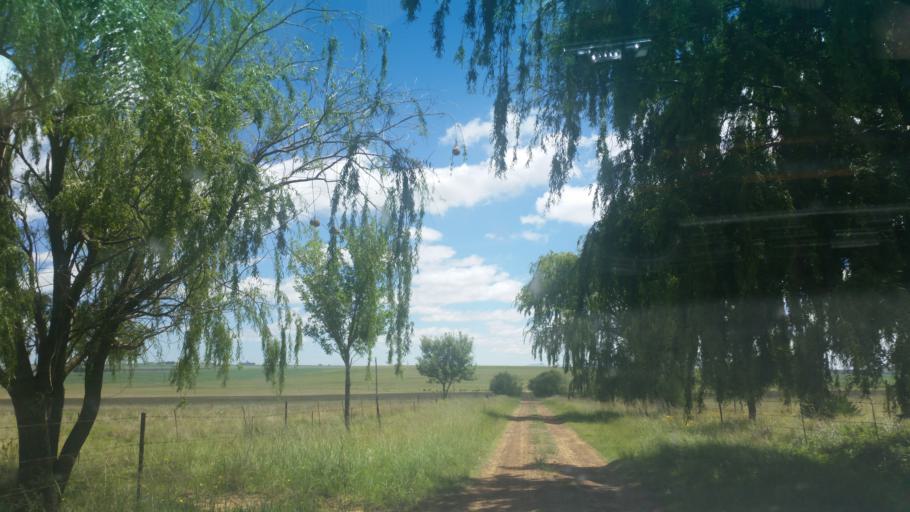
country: ZA
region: Orange Free State
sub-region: Thabo Mofutsanyana District Municipality
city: Harrismith
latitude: -28.1895
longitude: 29.0176
